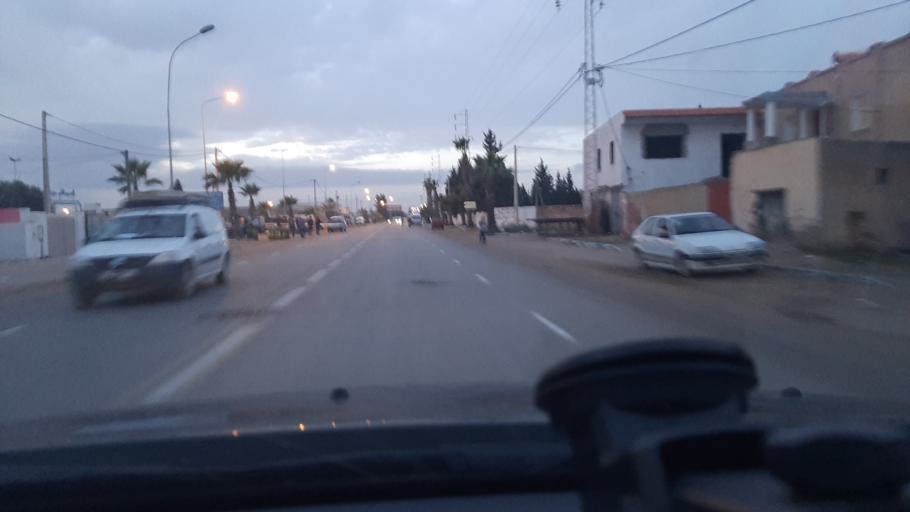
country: TN
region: Safaqis
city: Sfax
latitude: 34.7703
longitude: 10.6811
